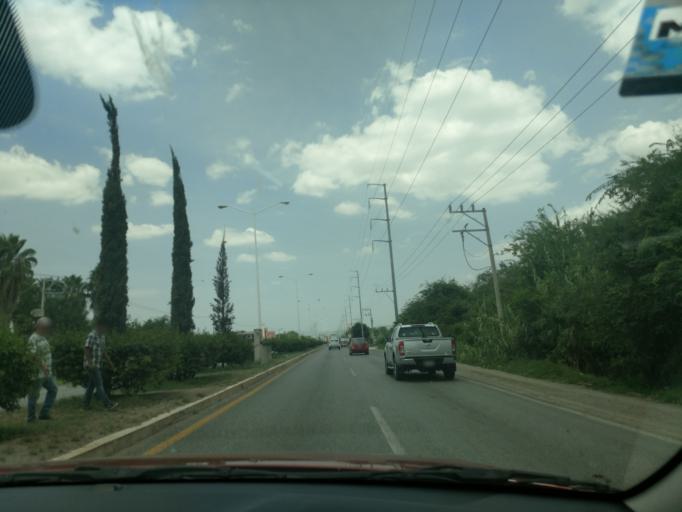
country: MX
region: San Luis Potosi
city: Rio Verde
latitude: 21.9226
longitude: -99.9850
